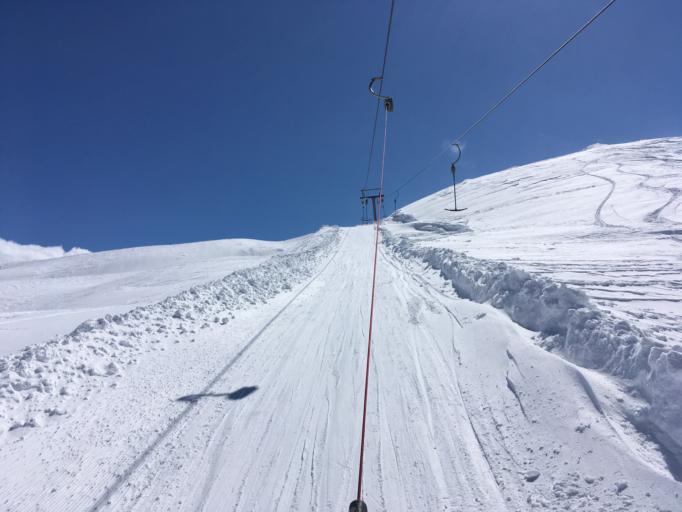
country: CH
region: Grisons
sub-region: Maloja District
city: Promontogno
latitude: 46.4409
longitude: 9.6366
